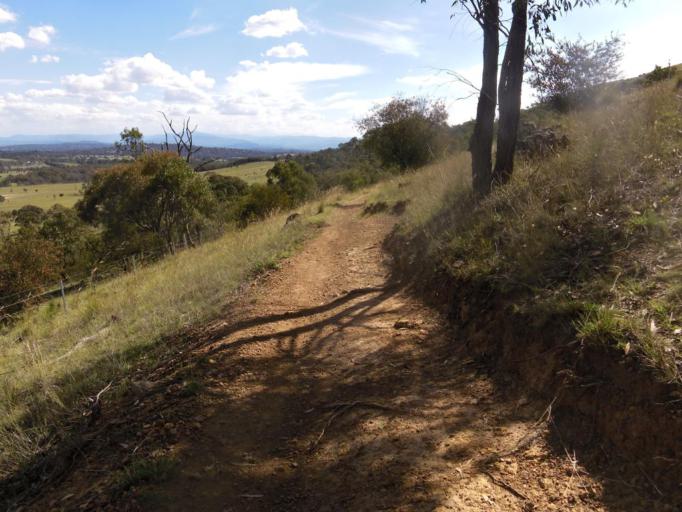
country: AU
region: Australian Capital Territory
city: Belconnen
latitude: -35.1570
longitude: 149.0807
